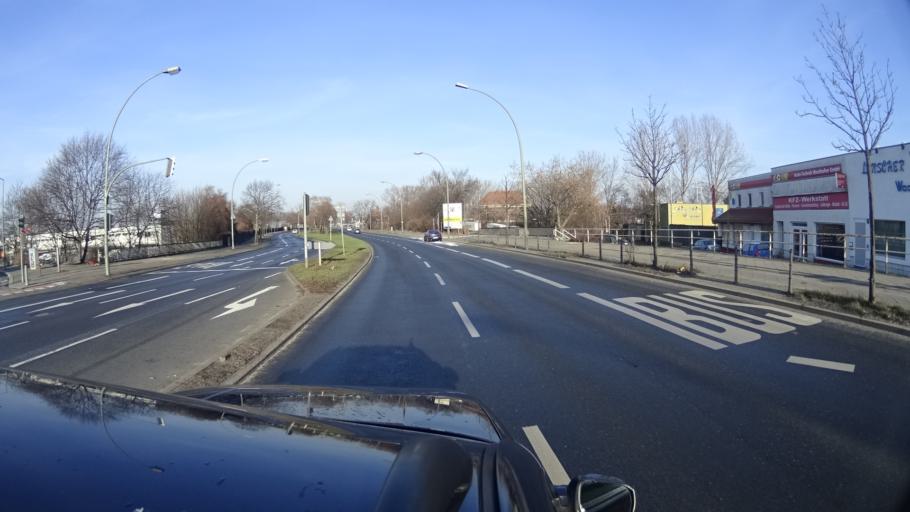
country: DE
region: Berlin
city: Moabit
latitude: 52.5348
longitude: 13.3284
